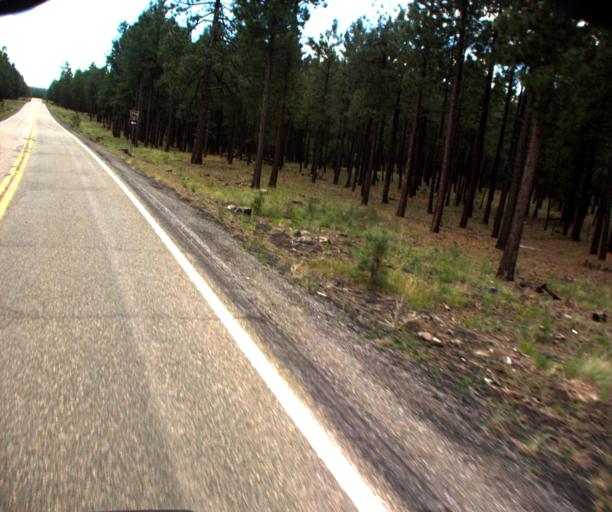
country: US
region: Arizona
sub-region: Coconino County
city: Parks
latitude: 35.3523
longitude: -111.7911
